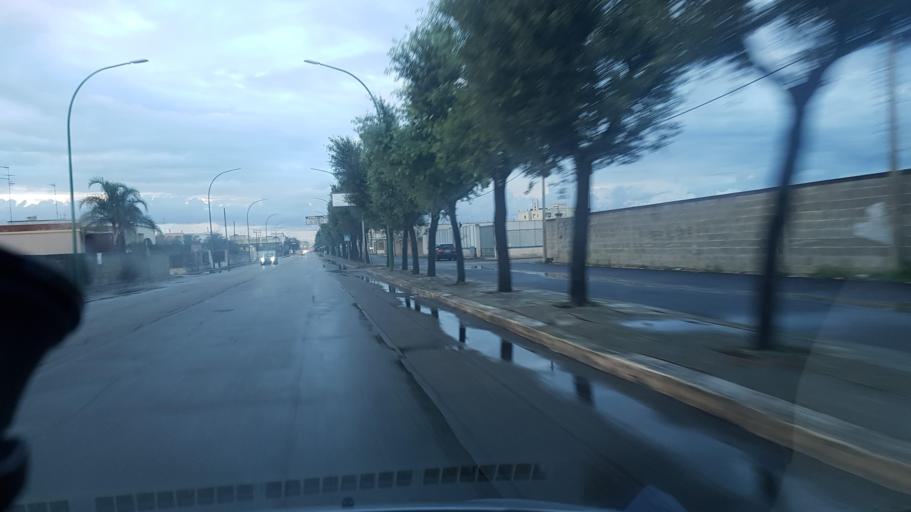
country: IT
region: Apulia
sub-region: Provincia di Lecce
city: Surbo
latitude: 40.3831
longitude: 18.1360
